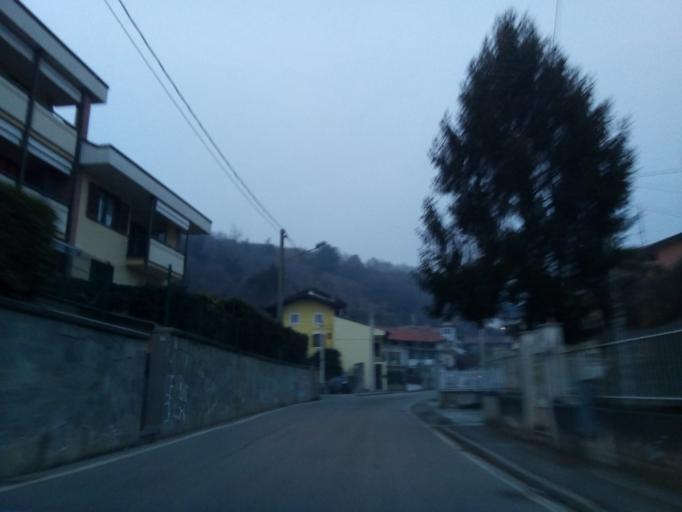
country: IT
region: Piedmont
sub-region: Provincia di Torino
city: Ivrea
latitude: 45.4722
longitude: 7.8740
